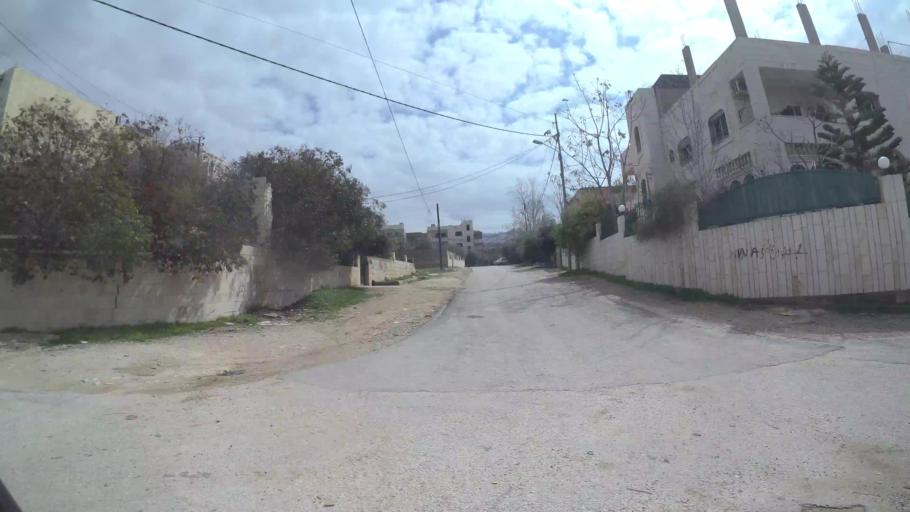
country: JO
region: Amman
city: Al Jubayhah
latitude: 32.0538
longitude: 35.8246
